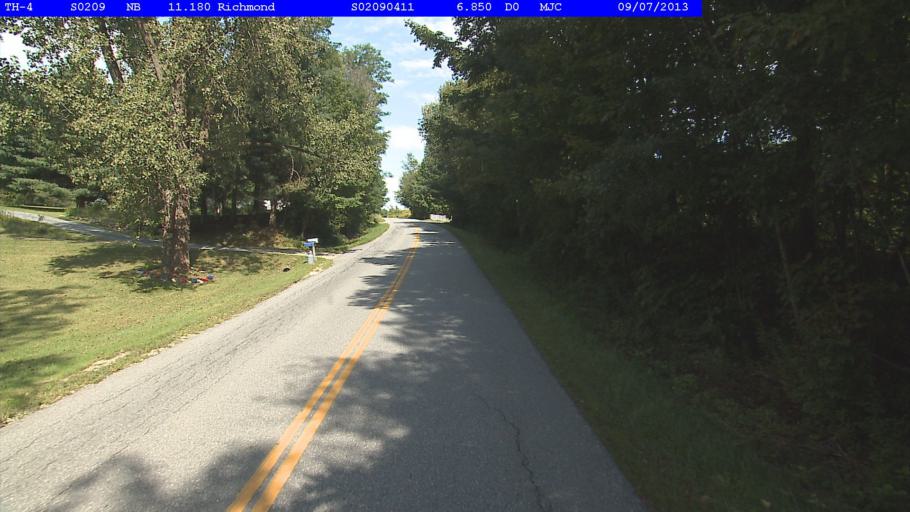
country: US
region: Vermont
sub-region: Chittenden County
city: Jericho
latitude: 44.4231
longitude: -72.9789
